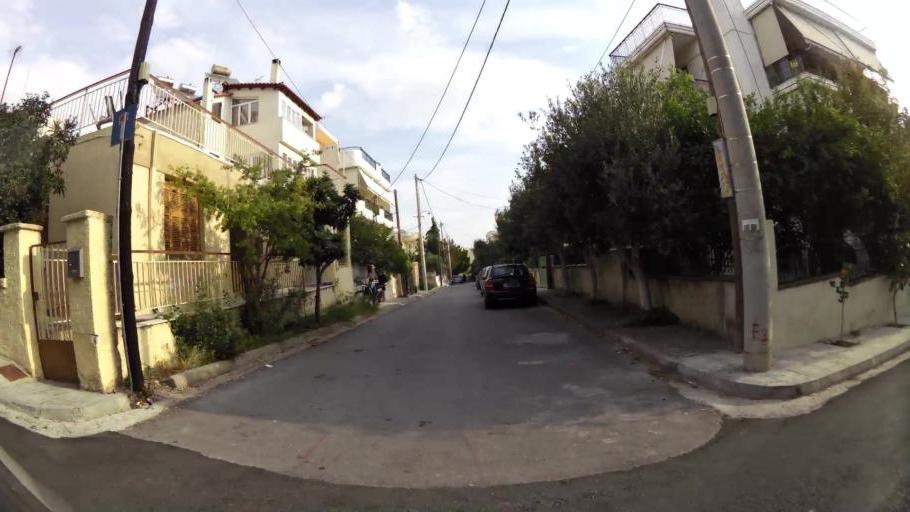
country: GR
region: Attica
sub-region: Nomarchia Athinas
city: Kamateron
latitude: 38.0543
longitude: 23.6963
